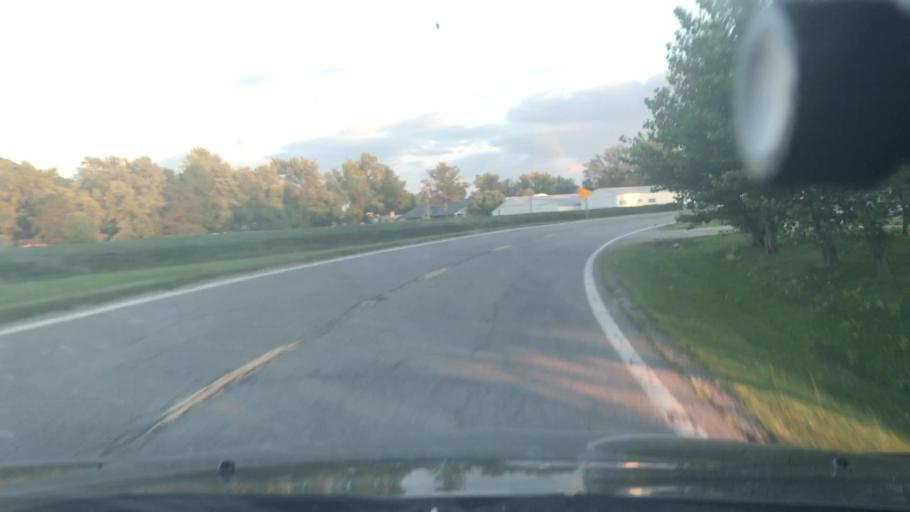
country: US
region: Illinois
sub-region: Washington County
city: Okawville
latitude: 38.3947
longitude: -89.4926
